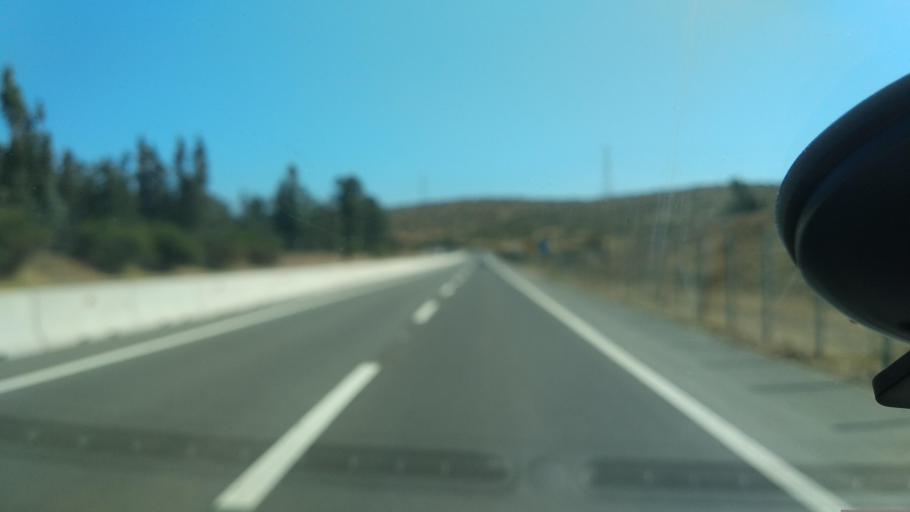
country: CL
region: Valparaiso
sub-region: Provincia de Marga Marga
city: Limache
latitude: -32.9921
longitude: -71.3285
